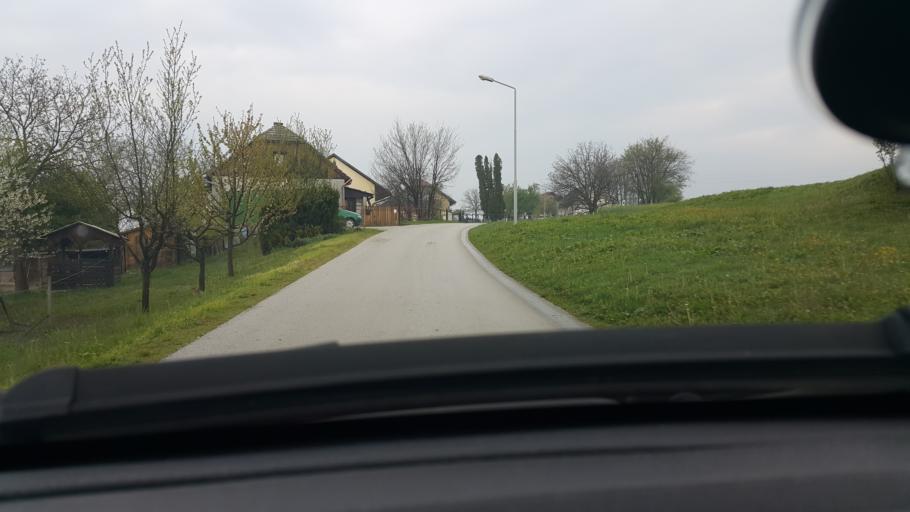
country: SI
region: Brezice
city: Brezice
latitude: 45.9013
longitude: 15.6542
